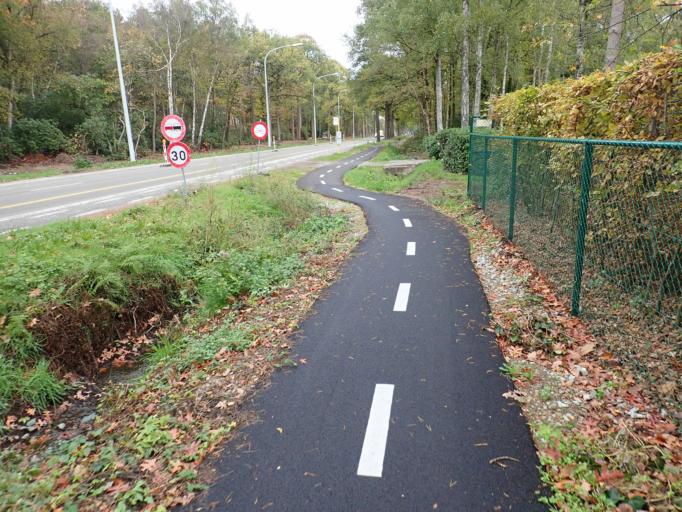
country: BE
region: Flanders
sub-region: Provincie Antwerpen
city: Brasschaat
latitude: 51.3423
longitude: 4.5333
